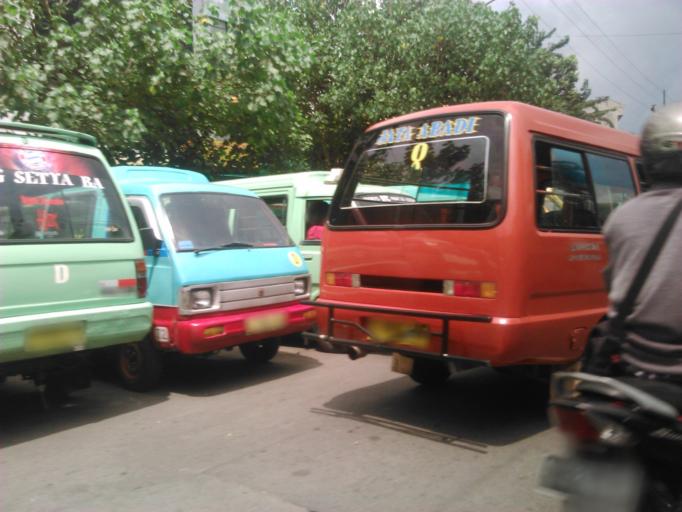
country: ID
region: East Java
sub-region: Kota Surabaya
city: Surabaya
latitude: -7.2467
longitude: 112.7334
